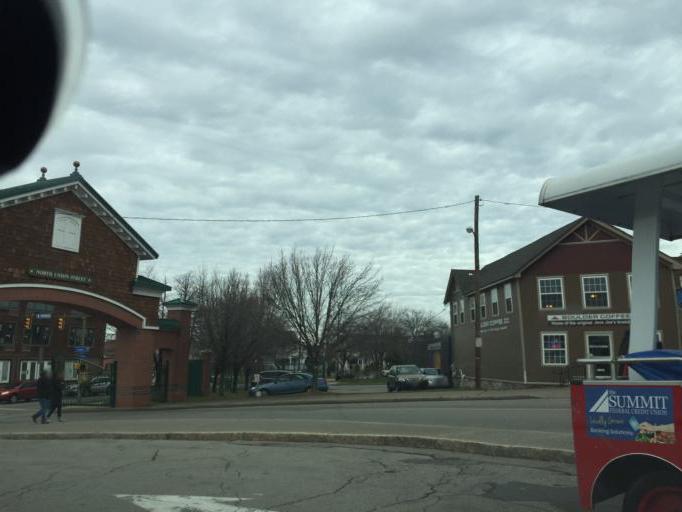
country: US
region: New York
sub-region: Monroe County
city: Rochester
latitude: 43.1657
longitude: -77.5906
